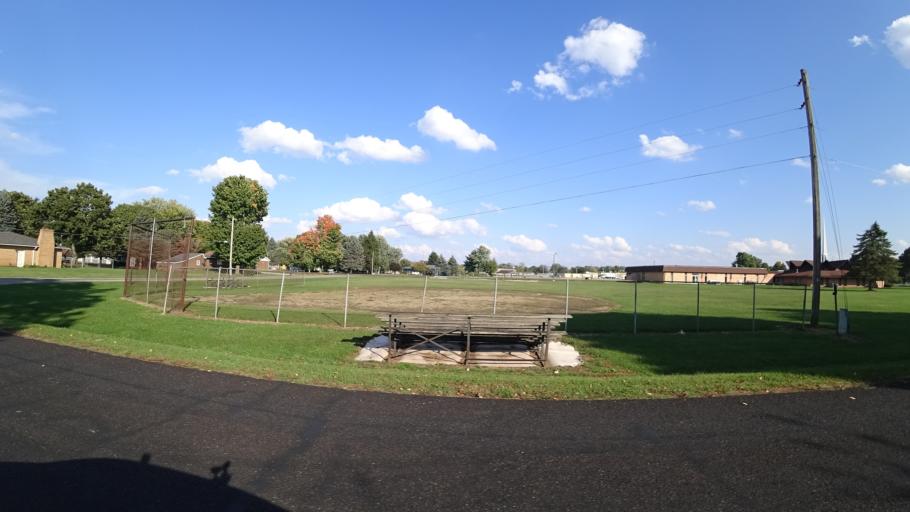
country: US
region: Michigan
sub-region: Saint Joseph County
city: Three Rivers
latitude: 41.9507
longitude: -85.6516
